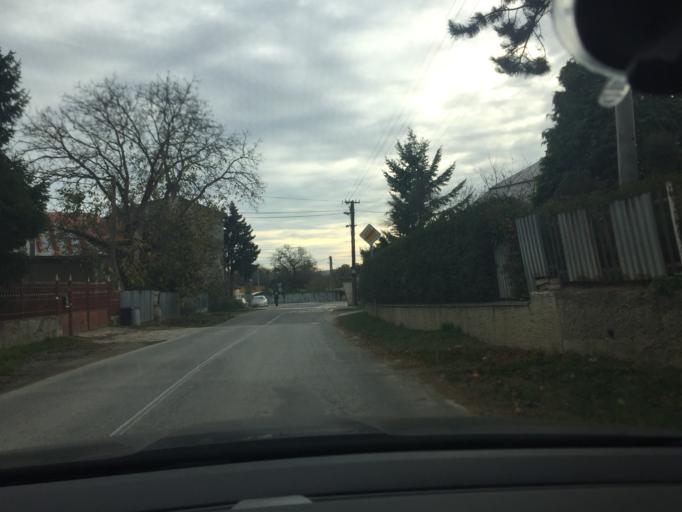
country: SK
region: Kosicky
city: Kosice
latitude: 48.8158
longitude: 21.3255
